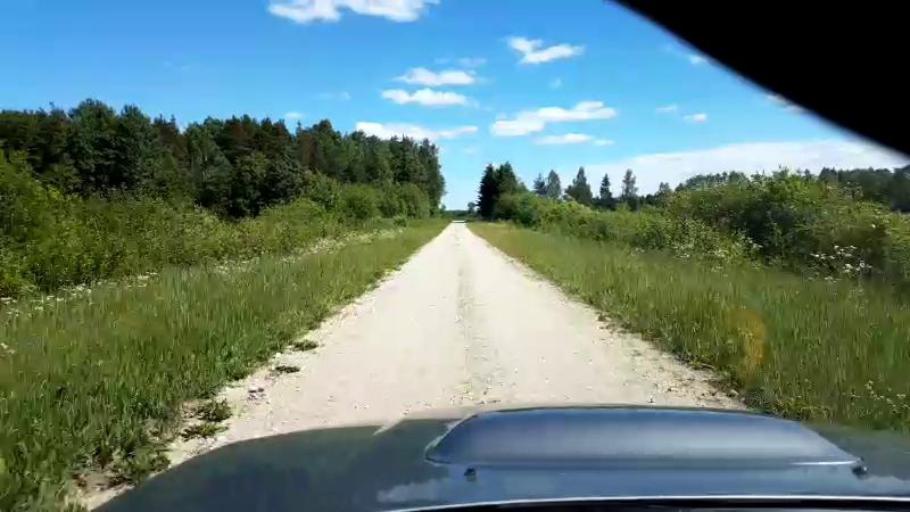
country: EE
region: Paernumaa
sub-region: Halinga vald
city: Parnu-Jaagupi
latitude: 58.5317
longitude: 24.5396
